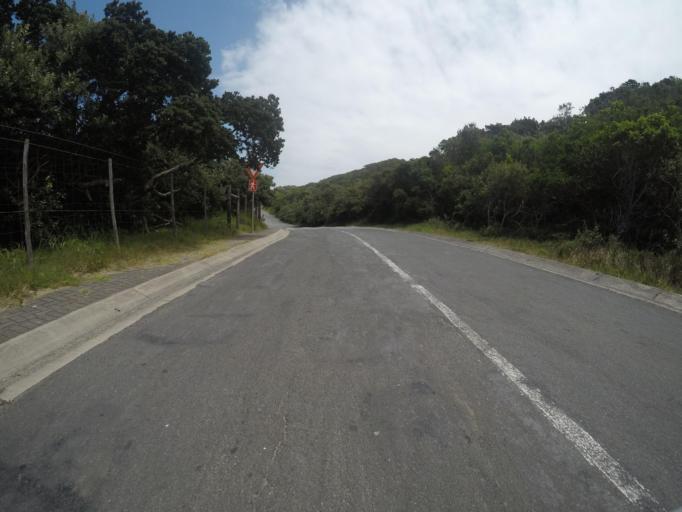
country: ZA
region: Eastern Cape
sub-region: Buffalo City Metropolitan Municipality
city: East London
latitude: -32.9947
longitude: 27.9482
